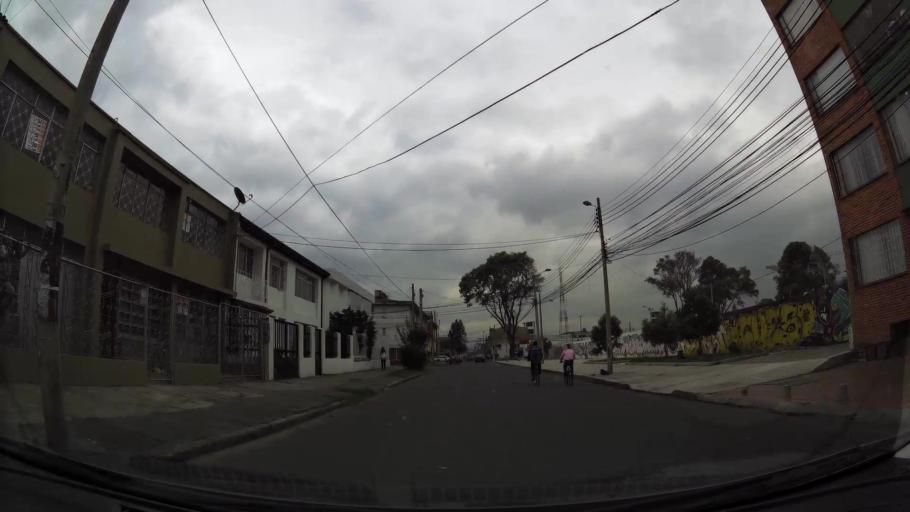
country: CO
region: Bogota D.C.
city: Barrio San Luis
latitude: 4.6634
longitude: -74.0660
